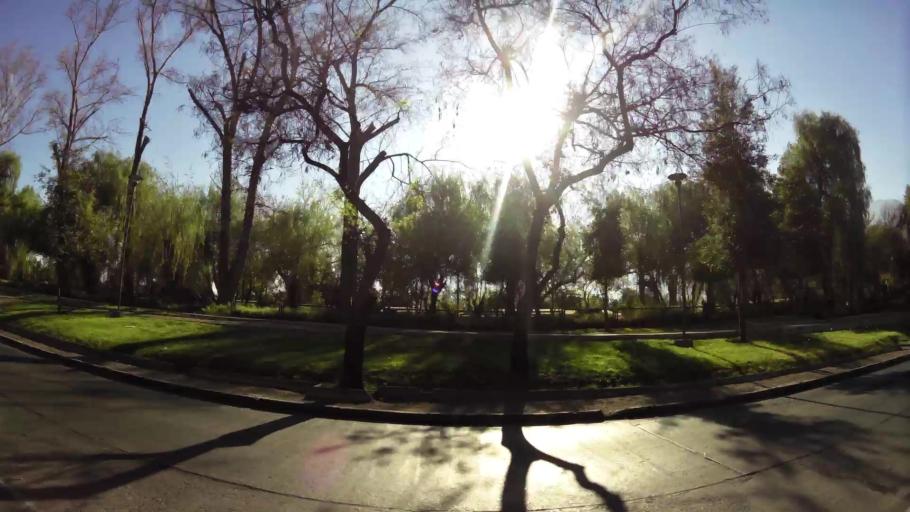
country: CL
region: Santiago Metropolitan
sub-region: Provincia de Santiago
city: Villa Presidente Frei, Nunoa, Santiago, Chile
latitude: -33.4575
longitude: -70.5552
